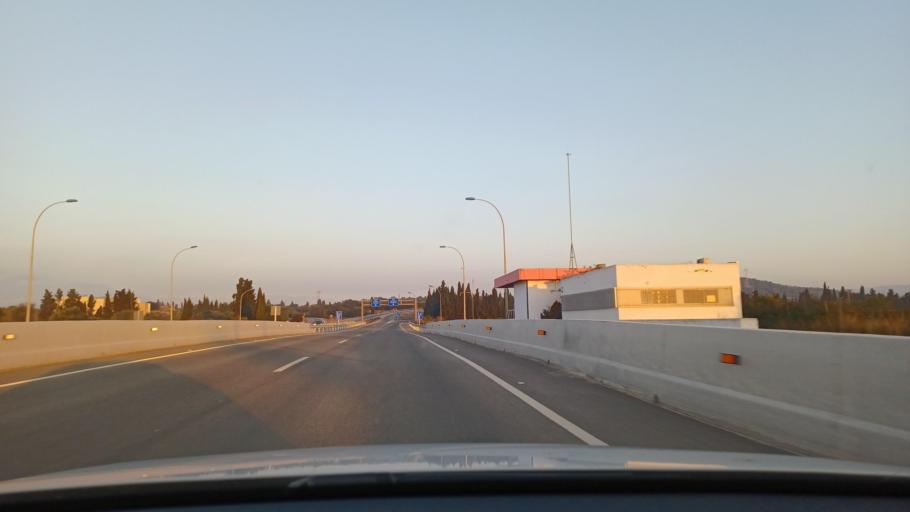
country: ES
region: Catalonia
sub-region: Provincia de Tarragona
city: Amposta
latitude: 40.7272
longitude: 0.5885
